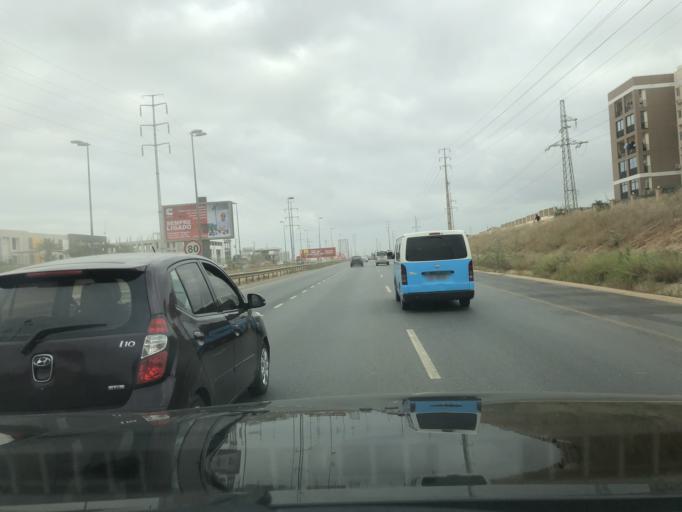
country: AO
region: Luanda
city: Luanda
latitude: -8.9741
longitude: 13.2191
